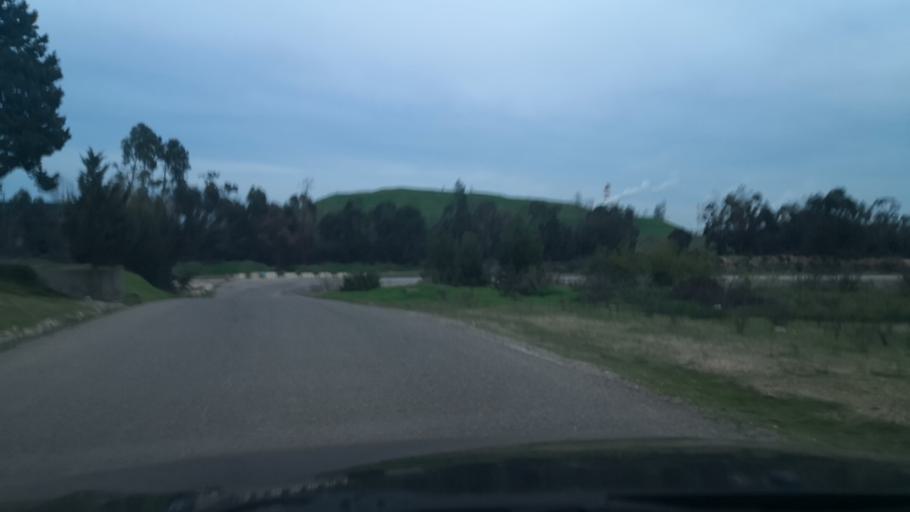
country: PT
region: Setubal
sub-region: Setubal
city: Setubal
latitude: 38.4974
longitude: -8.8211
